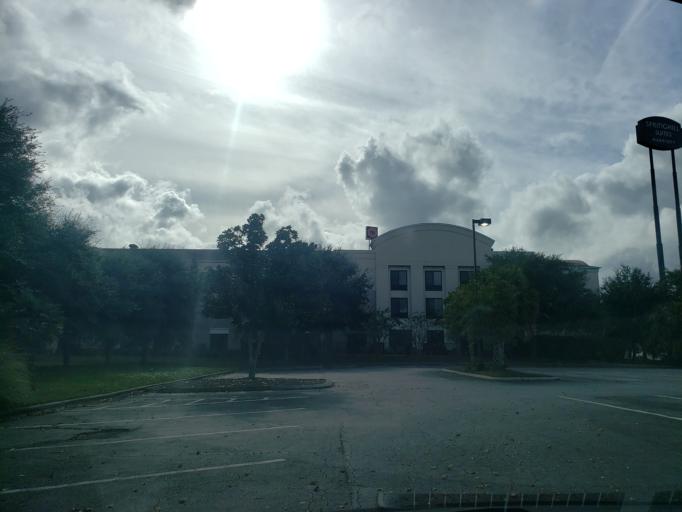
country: US
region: Georgia
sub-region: Chatham County
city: Georgetown
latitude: 32.0056
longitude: -81.2791
